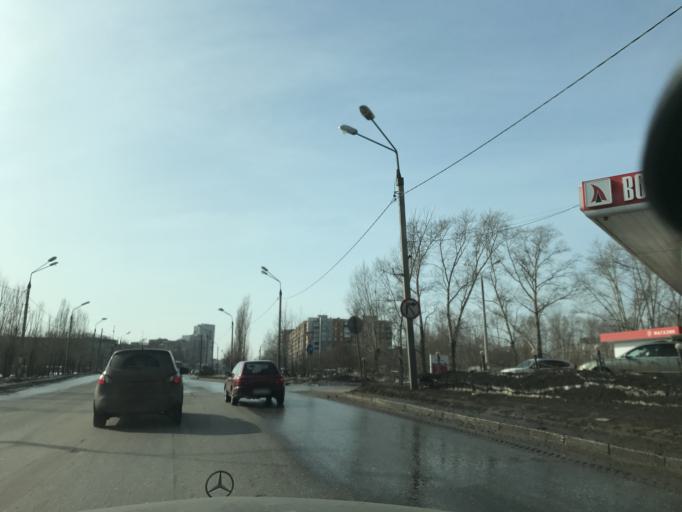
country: RU
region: Nizjnij Novgorod
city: Gorbatovka
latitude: 56.2630
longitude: 43.8672
